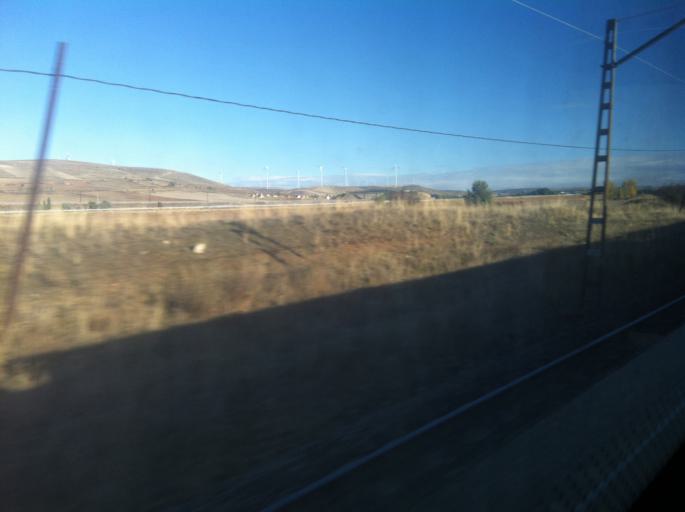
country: ES
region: Castille and Leon
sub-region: Provincia de Burgos
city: Villazopeque
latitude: 42.1900
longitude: -4.0312
